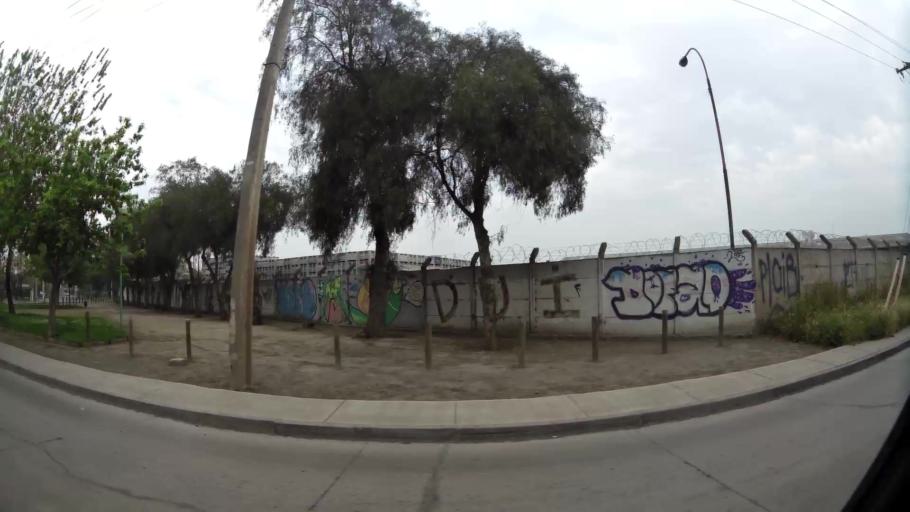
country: CL
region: Santiago Metropolitan
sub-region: Provincia de Santiago
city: Lo Prado
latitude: -33.4818
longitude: -70.7035
